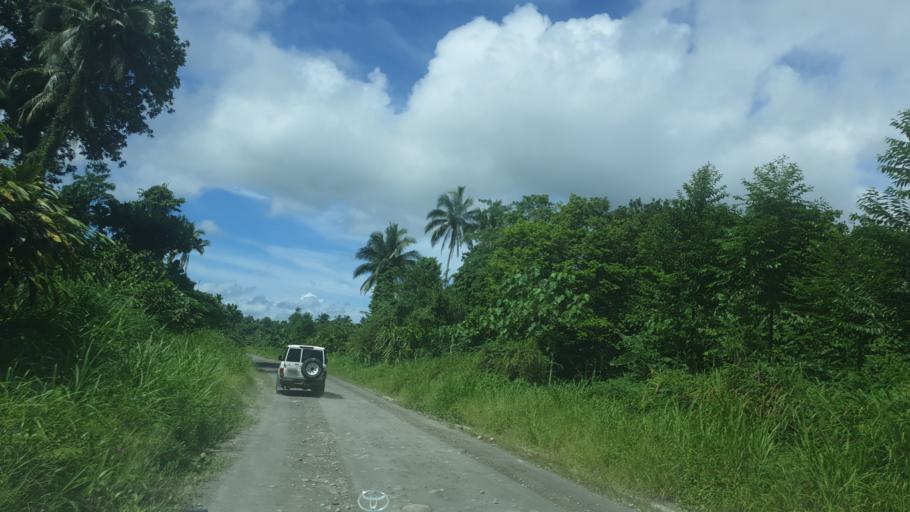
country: PG
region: Bougainville
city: Panguna
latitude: -6.5587
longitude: 155.3542
